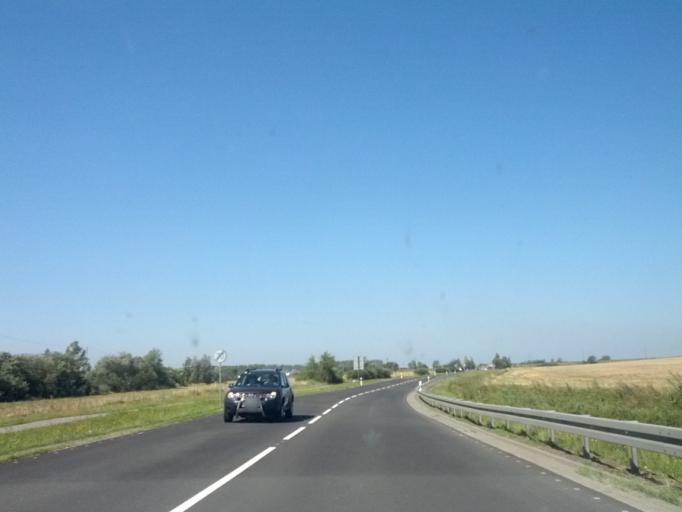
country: DE
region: Mecklenburg-Vorpommern
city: Sagard
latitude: 54.5055
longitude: 13.5469
